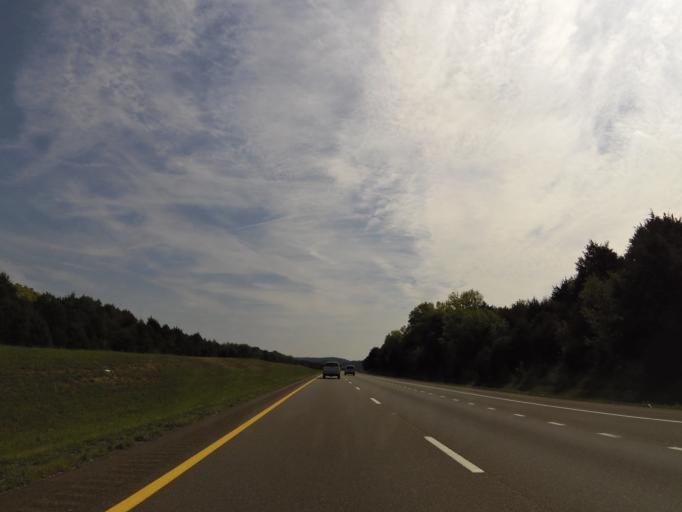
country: US
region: Tennessee
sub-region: Hamblen County
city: Morristown
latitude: 36.1947
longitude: -83.1688
